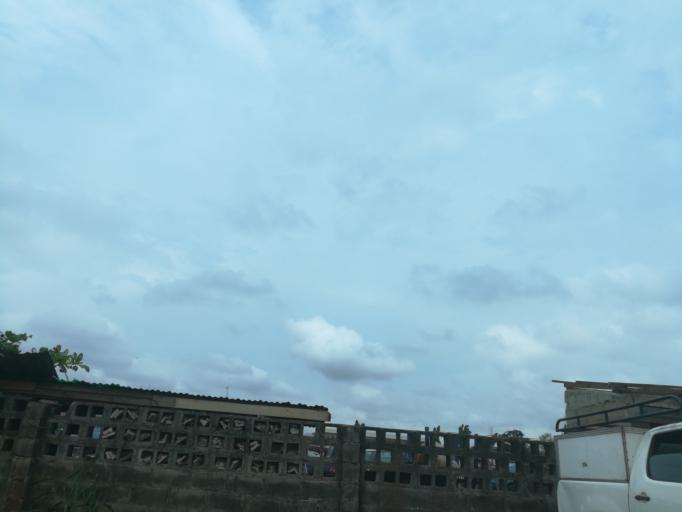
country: NG
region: Lagos
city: Oshodi
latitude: 6.5660
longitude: 3.3220
